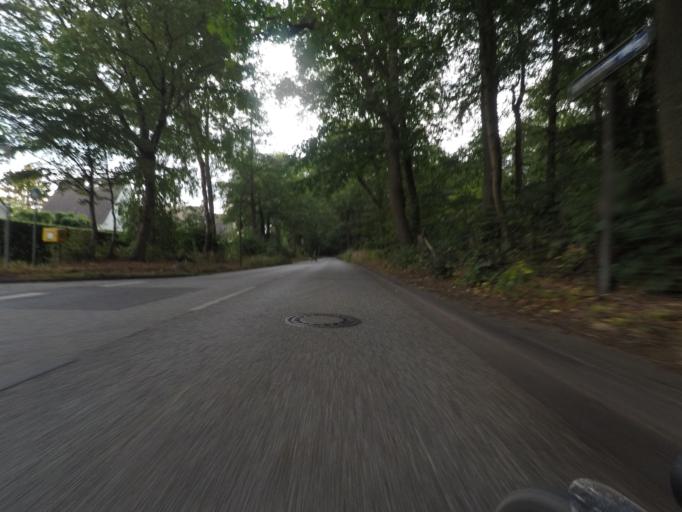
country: DE
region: Hamburg
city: Sasel
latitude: 53.6463
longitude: 10.1322
